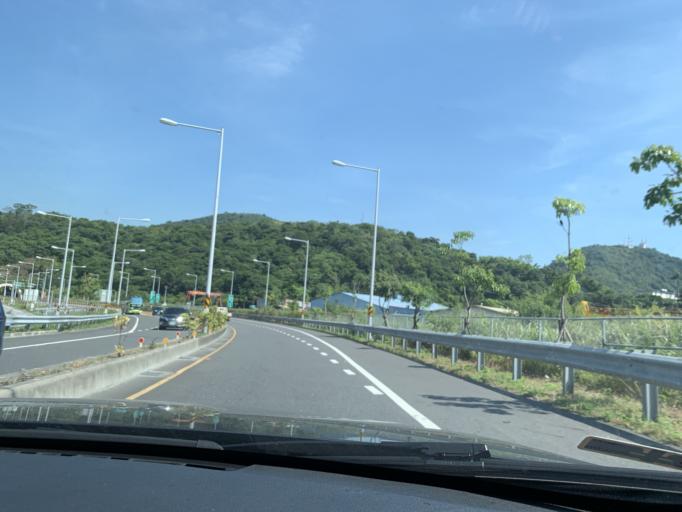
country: TW
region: Taiwan
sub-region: Yilan
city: Yilan
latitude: 24.5898
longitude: 121.8494
